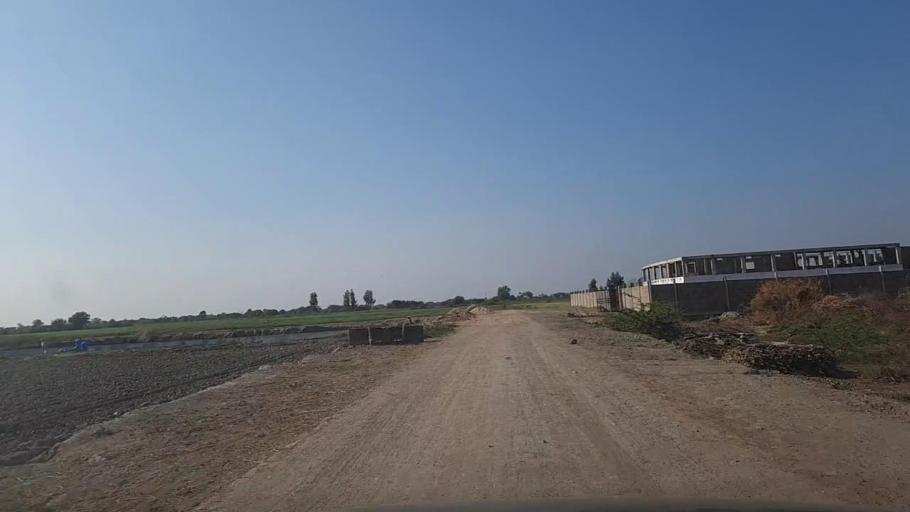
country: PK
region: Sindh
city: Digri
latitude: 25.0278
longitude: 69.2243
